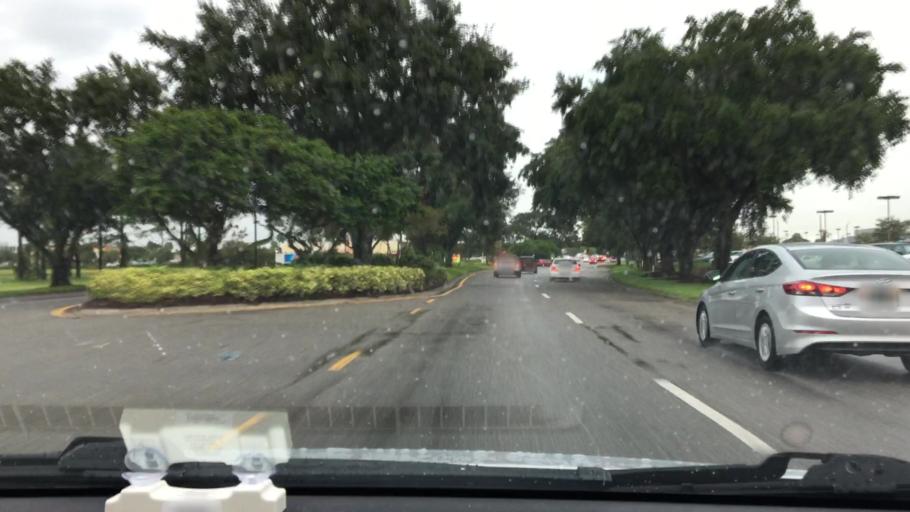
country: US
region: Florida
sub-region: Orange County
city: Conway
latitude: 28.4688
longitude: -81.3137
